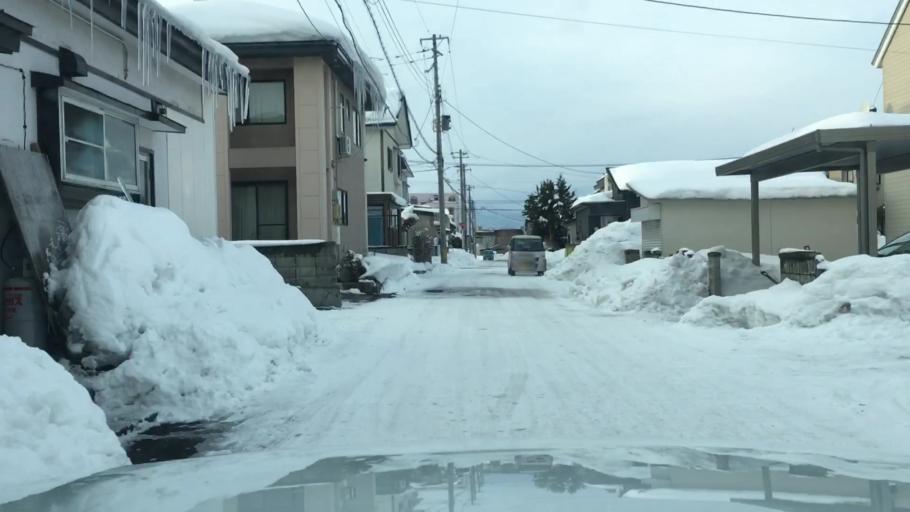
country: JP
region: Aomori
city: Hirosaki
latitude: 40.5794
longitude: 140.4887
